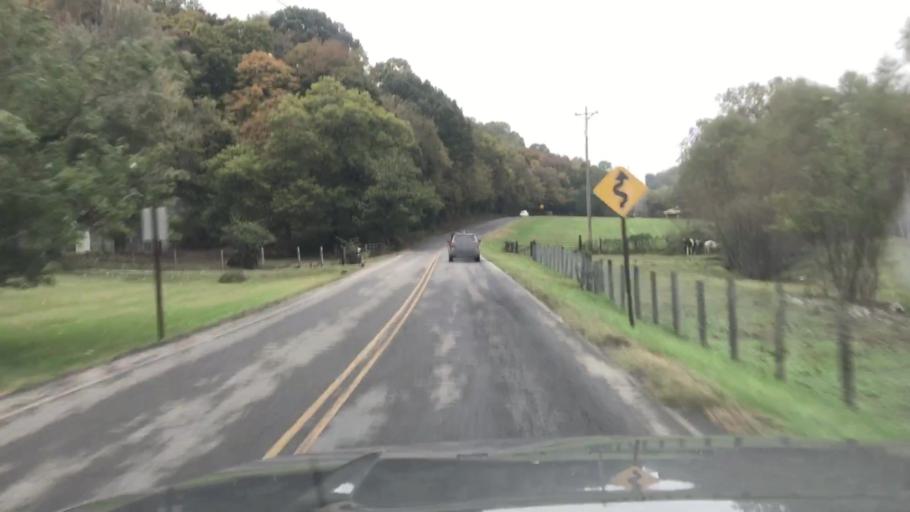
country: US
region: Tennessee
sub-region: Williamson County
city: Brentwood Estates
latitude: 35.9836
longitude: -86.8295
